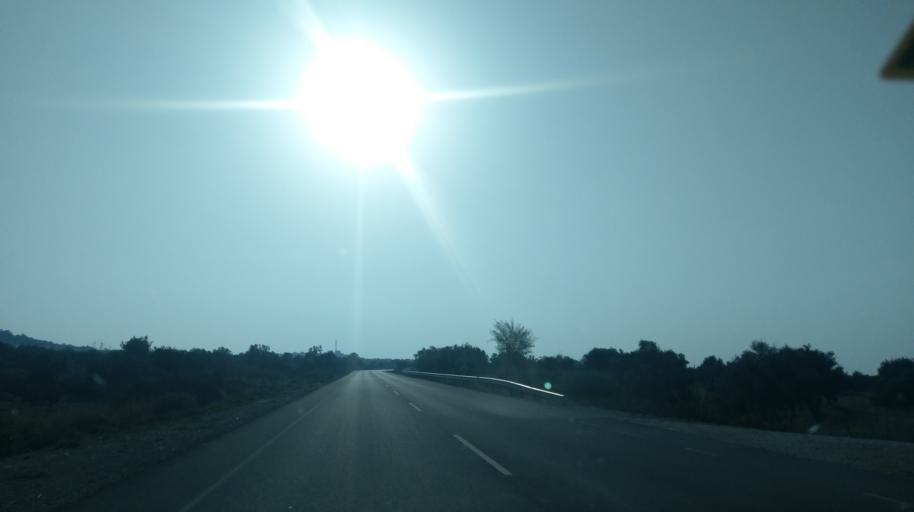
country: CY
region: Ammochostos
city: Leonarisso
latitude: 35.5516
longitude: 34.2095
